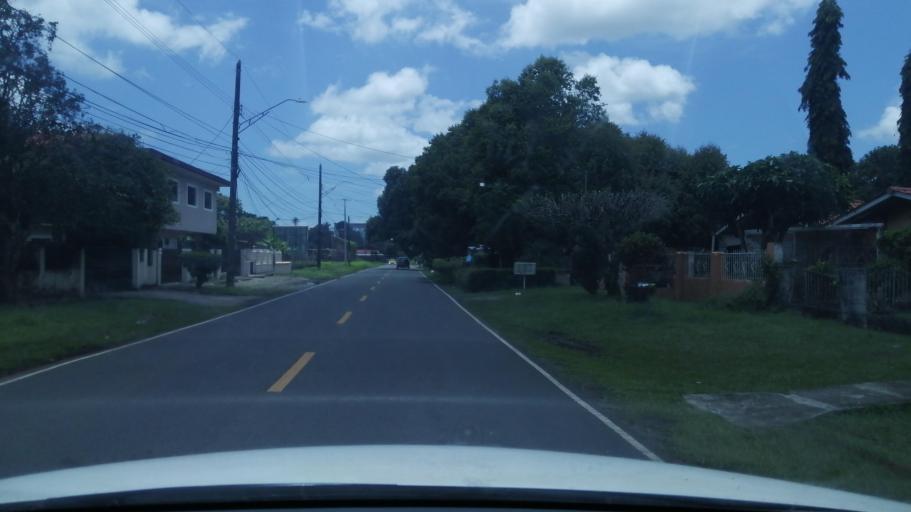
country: PA
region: Chiriqui
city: David
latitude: 8.4355
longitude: -82.4294
